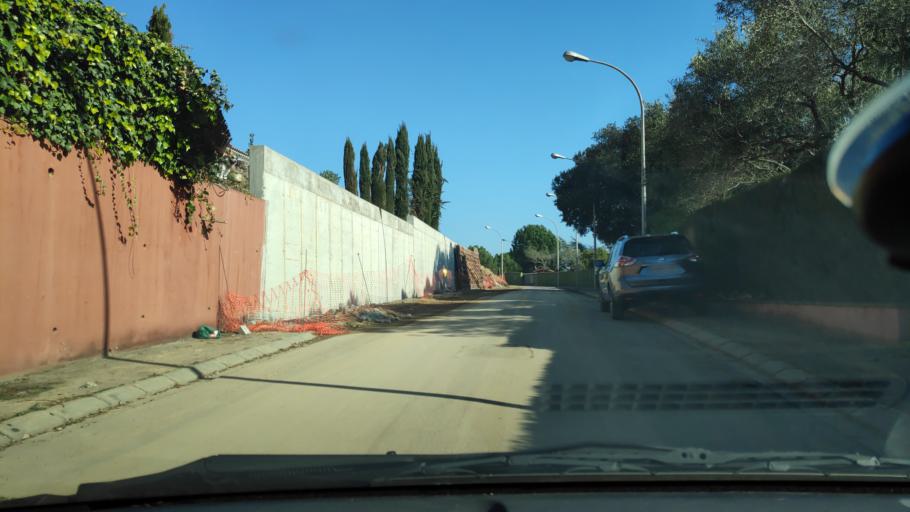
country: ES
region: Catalonia
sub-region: Provincia de Barcelona
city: Sant Quirze del Valles
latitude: 41.5077
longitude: 2.0818
